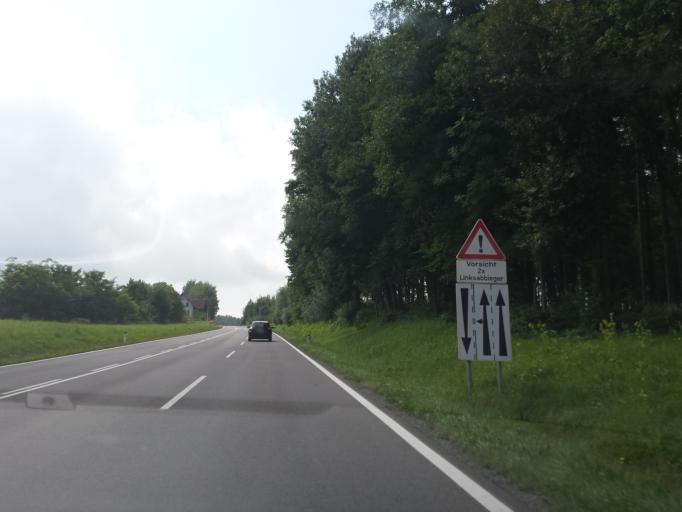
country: AT
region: Styria
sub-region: Politischer Bezirk Deutschlandsberg
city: Stainz
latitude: 46.8833
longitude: 15.2585
